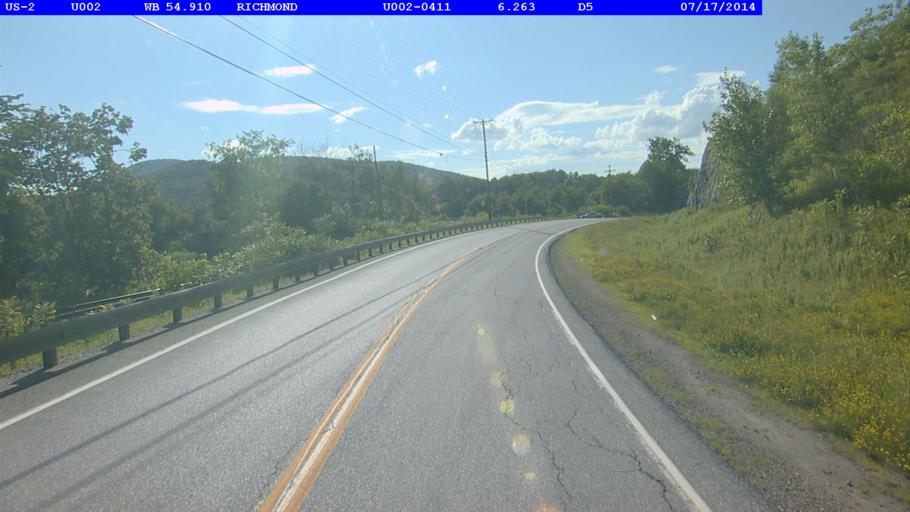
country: US
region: Vermont
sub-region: Chittenden County
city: Jericho
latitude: 44.3830
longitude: -72.9357
